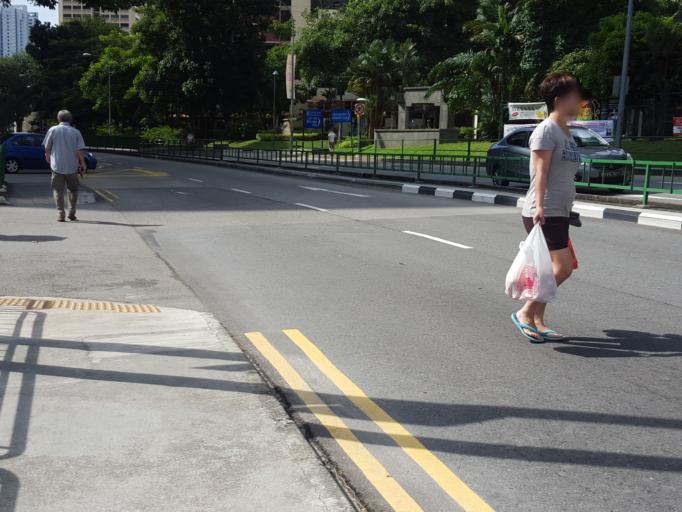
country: SG
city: Singapore
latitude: 1.3362
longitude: 103.8463
